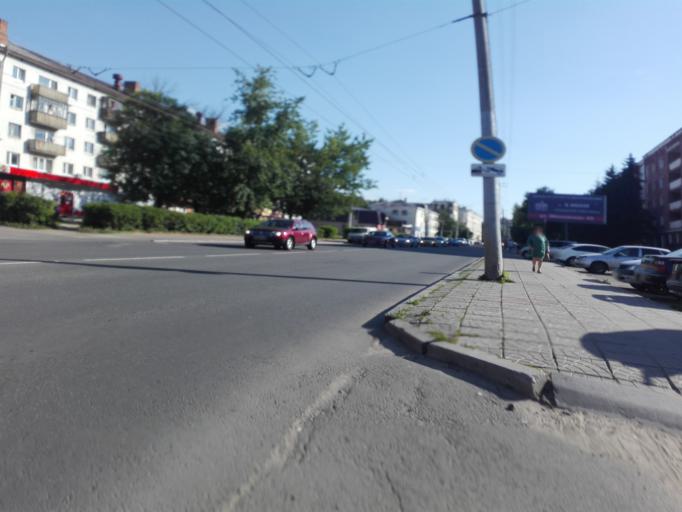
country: RU
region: Orjol
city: Orel
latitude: 52.9800
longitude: 36.0683
